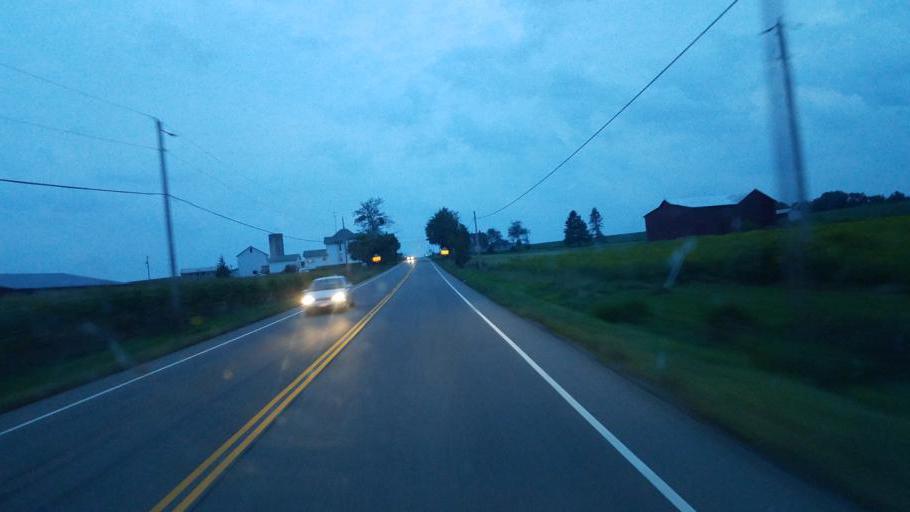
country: US
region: Ohio
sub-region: Knox County
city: Fredericktown
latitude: 40.5392
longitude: -82.5432
